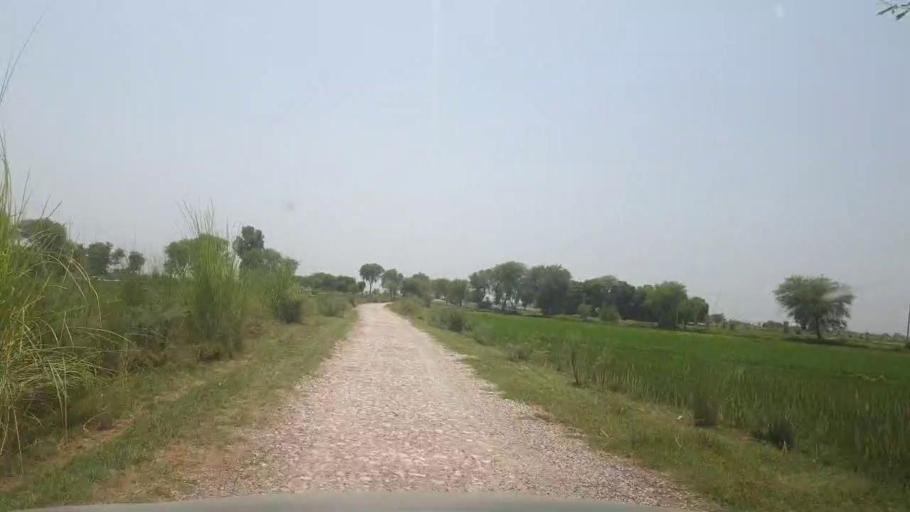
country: PK
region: Sindh
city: Lakhi
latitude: 27.8474
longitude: 68.6644
